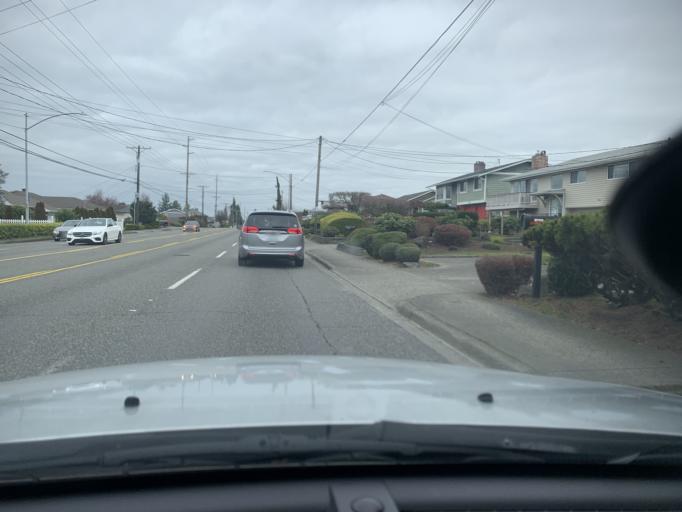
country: US
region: Washington
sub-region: Pierce County
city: University Place
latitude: 47.2440
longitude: -122.5370
